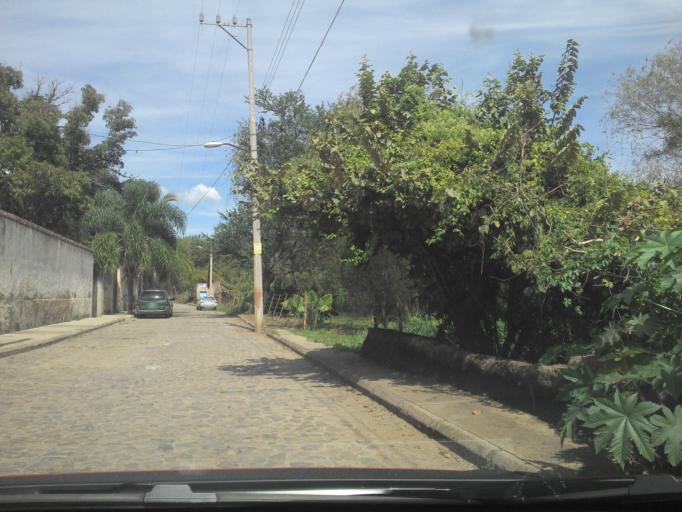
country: MX
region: Jalisco
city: Teuchitlan
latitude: 20.6876
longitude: -103.8448
